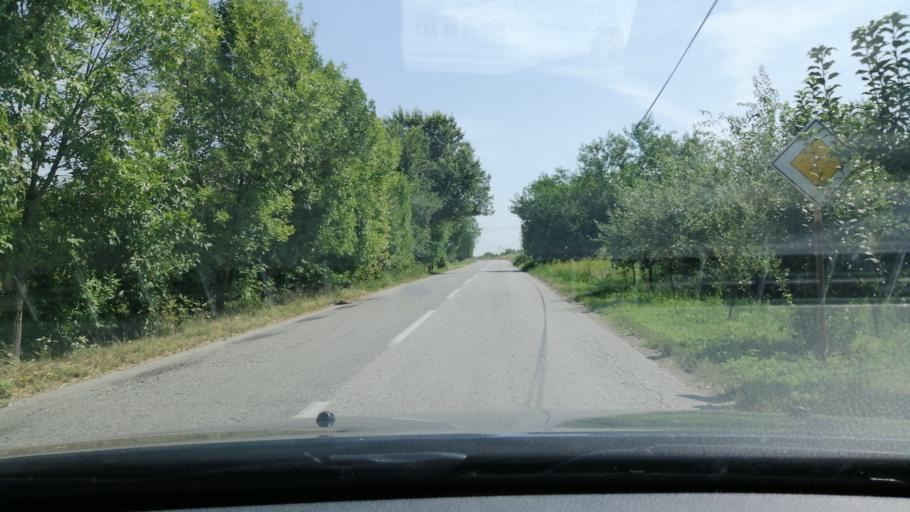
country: RS
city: Boka
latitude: 45.3551
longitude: 20.8375
